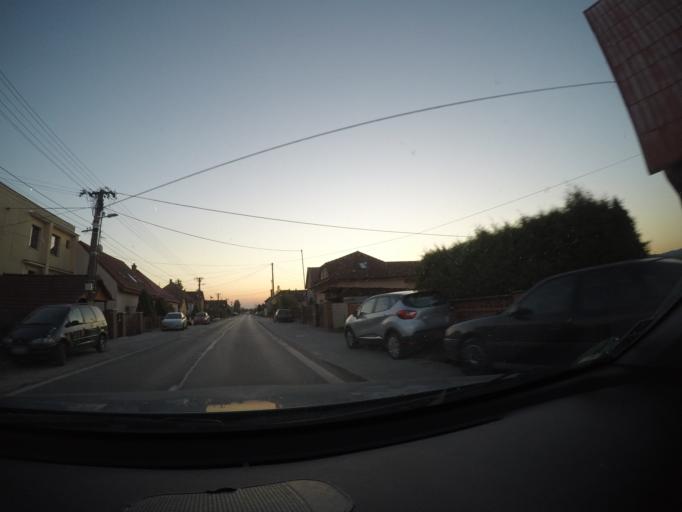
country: SK
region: Trenciansky
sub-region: Okres Trencin
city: Trencin
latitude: 48.9074
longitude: 18.0475
